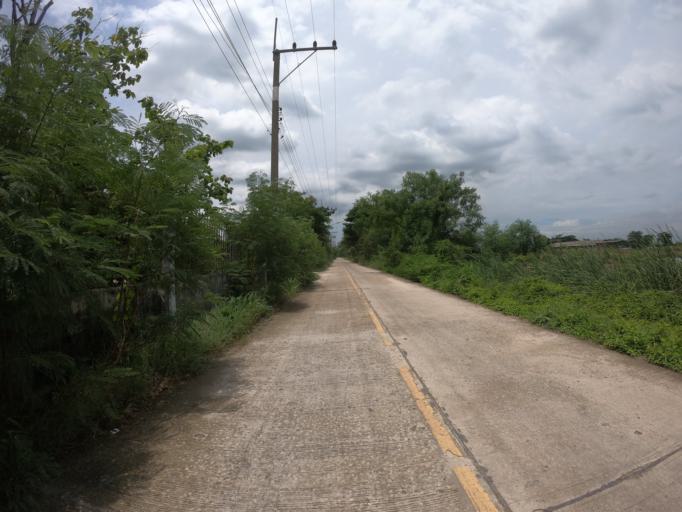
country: TH
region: Pathum Thani
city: Ban Lam Luk Ka
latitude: 13.9900
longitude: 100.8562
